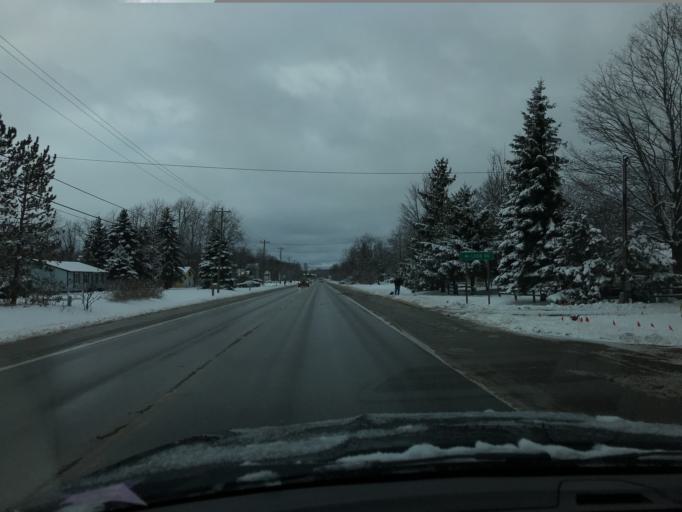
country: US
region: Michigan
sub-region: Charlevoix County
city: Charlevoix
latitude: 45.2907
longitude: -85.2480
